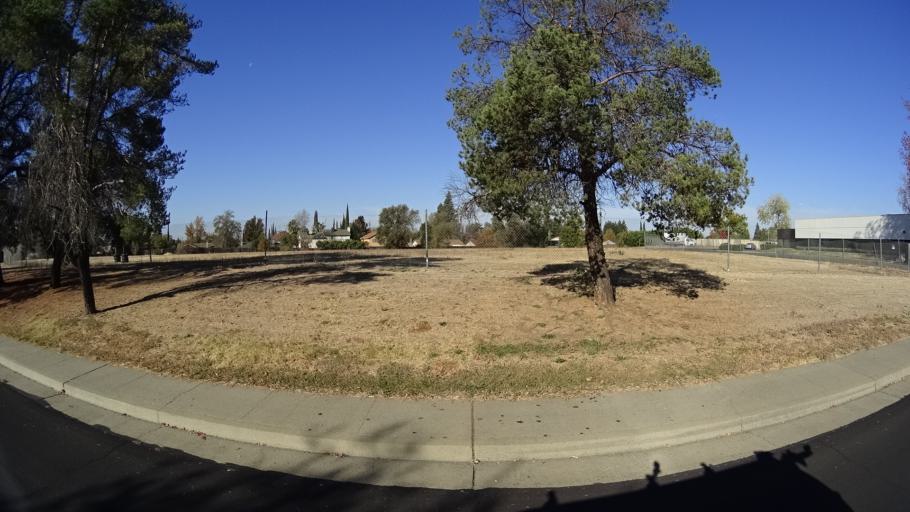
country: US
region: California
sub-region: Sacramento County
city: Citrus Heights
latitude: 38.7226
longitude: -121.2935
